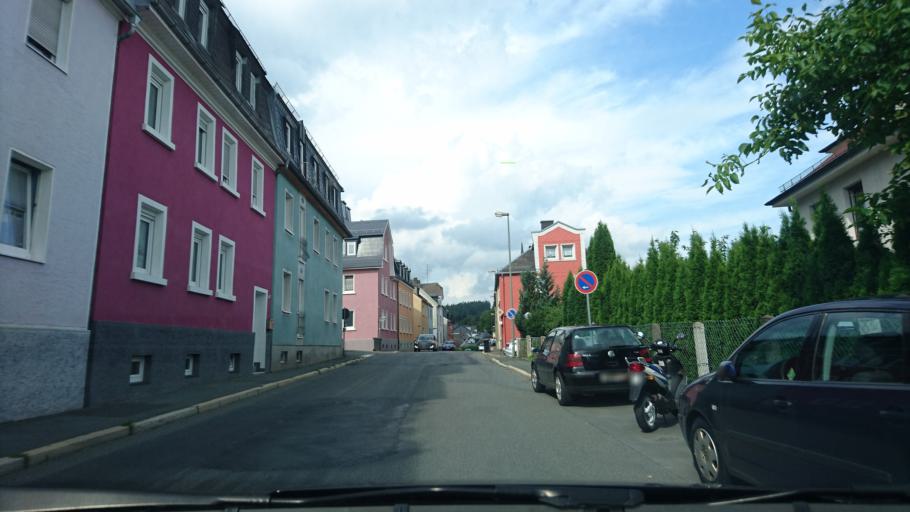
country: DE
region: Bavaria
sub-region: Upper Franconia
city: Naila
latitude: 50.3278
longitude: 11.7046
